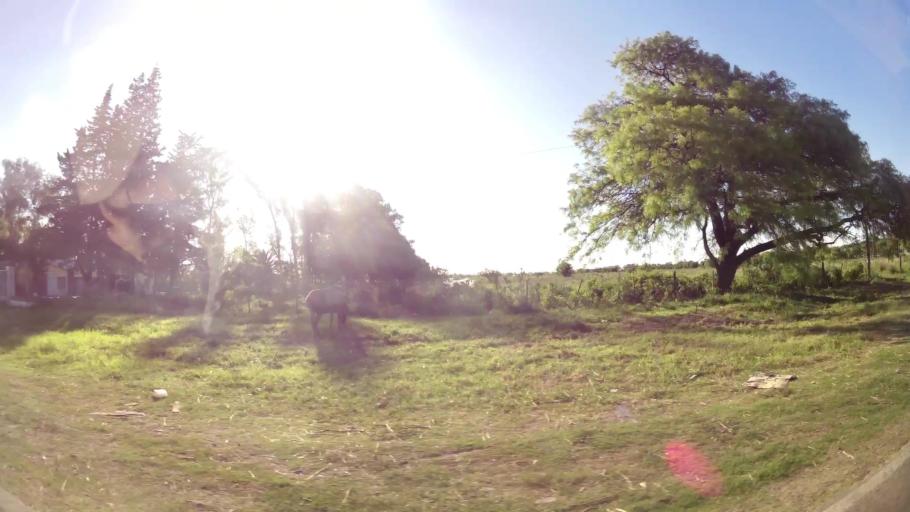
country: AR
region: Cordoba
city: San Francisco
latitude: -31.4447
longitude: -62.1007
